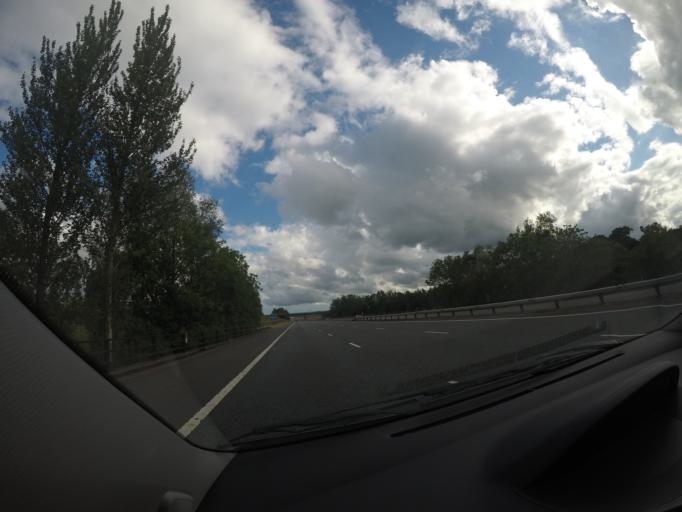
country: GB
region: Scotland
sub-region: Dumfries and Galloway
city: Lochmaben
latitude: 55.2124
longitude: -3.4125
